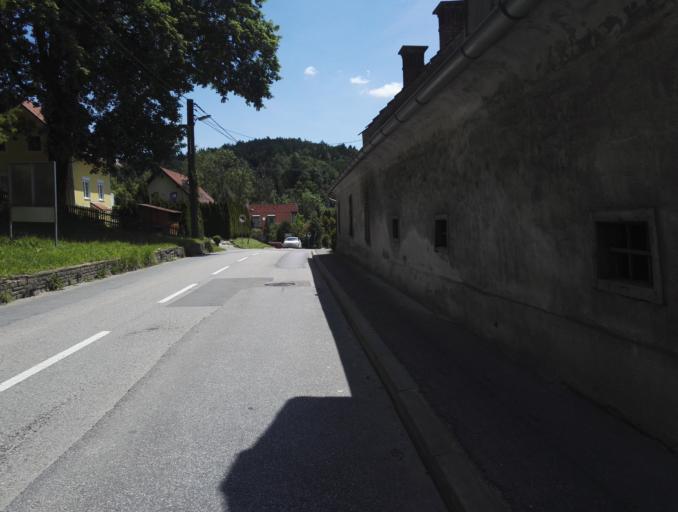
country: AT
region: Styria
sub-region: Politischer Bezirk Graz-Umgebung
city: Grambach
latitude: 47.0175
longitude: 15.5030
